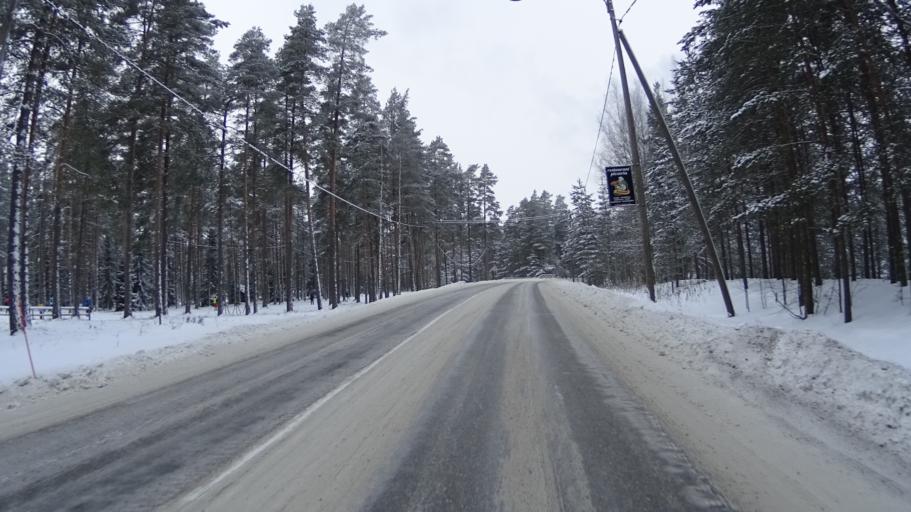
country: FI
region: Uusimaa
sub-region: Helsinki
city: Vihti
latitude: 60.3381
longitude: 24.3109
